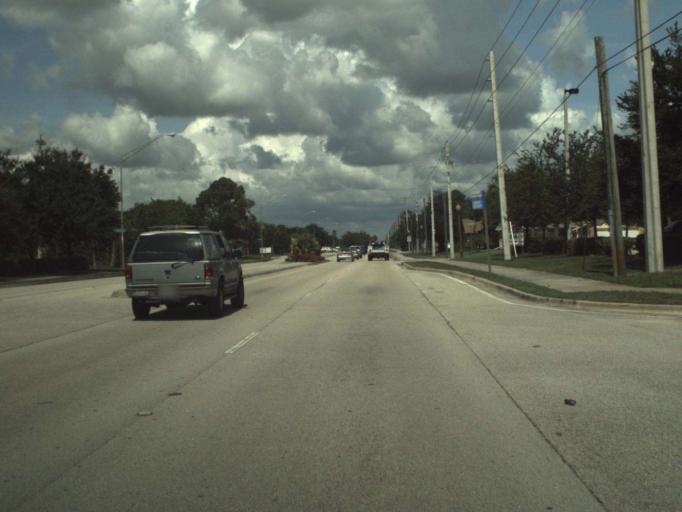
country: US
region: Florida
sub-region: Saint Lucie County
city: River Park
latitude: 27.3178
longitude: -80.3592
